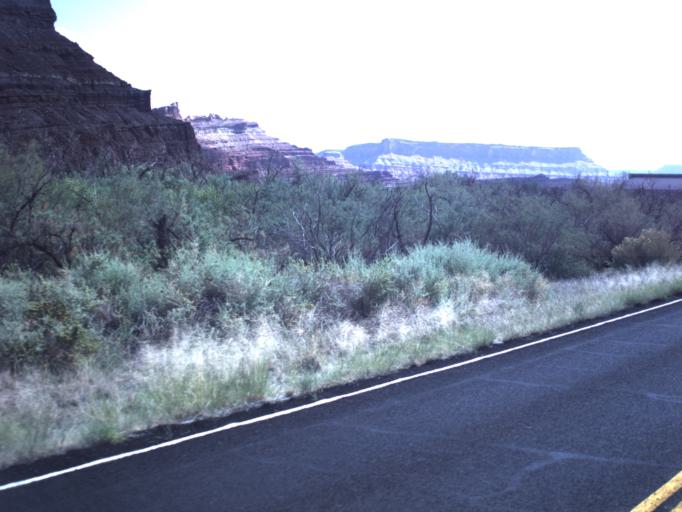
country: US
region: Utah
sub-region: Grand County
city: Moab
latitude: 38.5333
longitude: -109.6564
